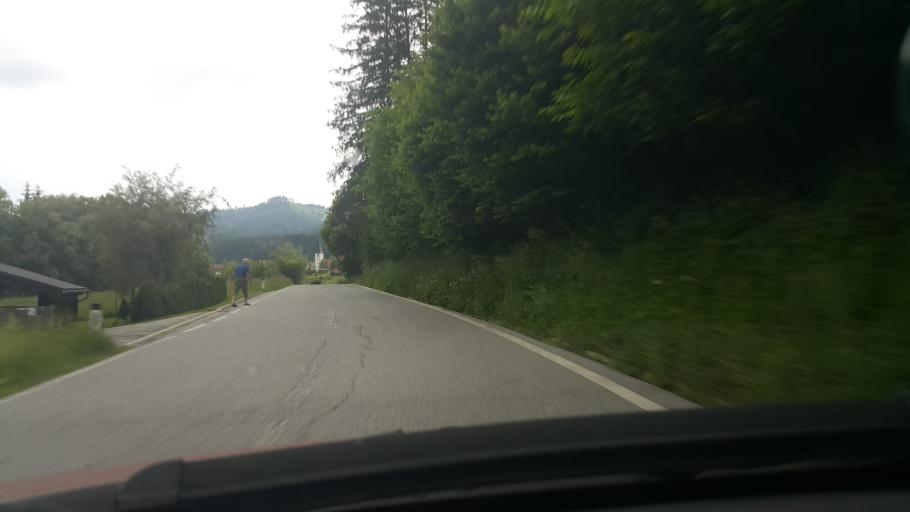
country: AT
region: Styria
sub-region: Politischer Bezirk Graz-Umgebung
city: Stiwoll
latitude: 47.0979
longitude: 15.2202
